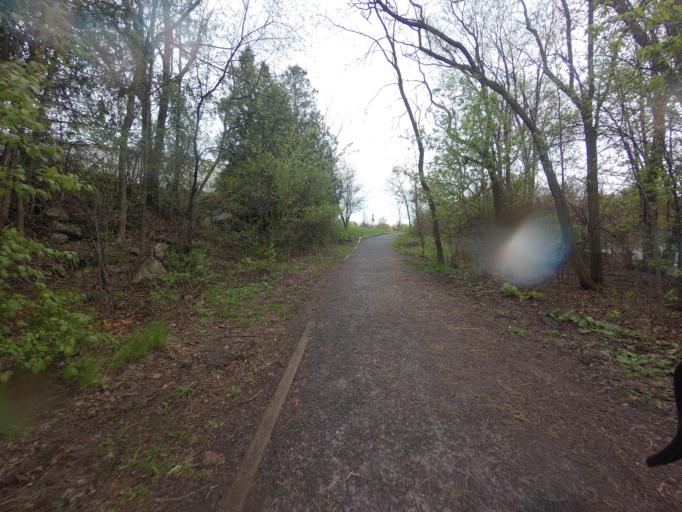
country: CA
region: Ontario
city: Carleton Place
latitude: 45.1433
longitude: -76.1394
